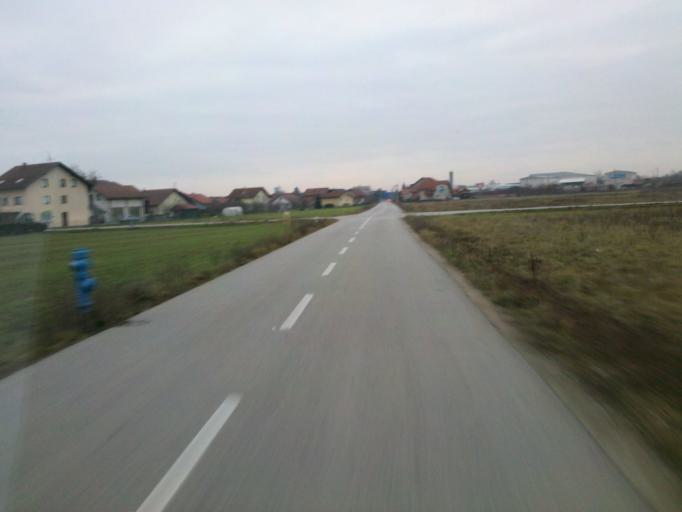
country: HR
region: Grad Zagreb
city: Lucko
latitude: 45.7578
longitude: 15.8732
